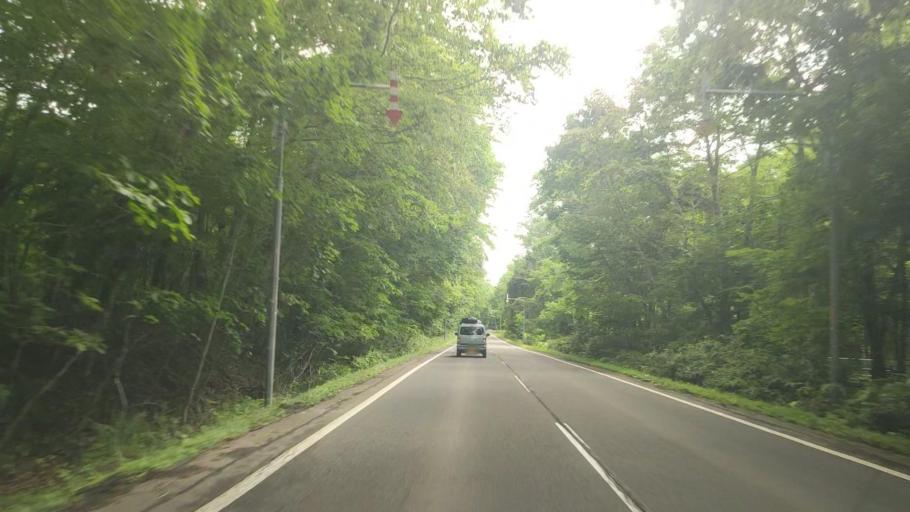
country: JP
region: Hokkaido
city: Tomakomai
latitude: 42.7771
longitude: 141.4408
